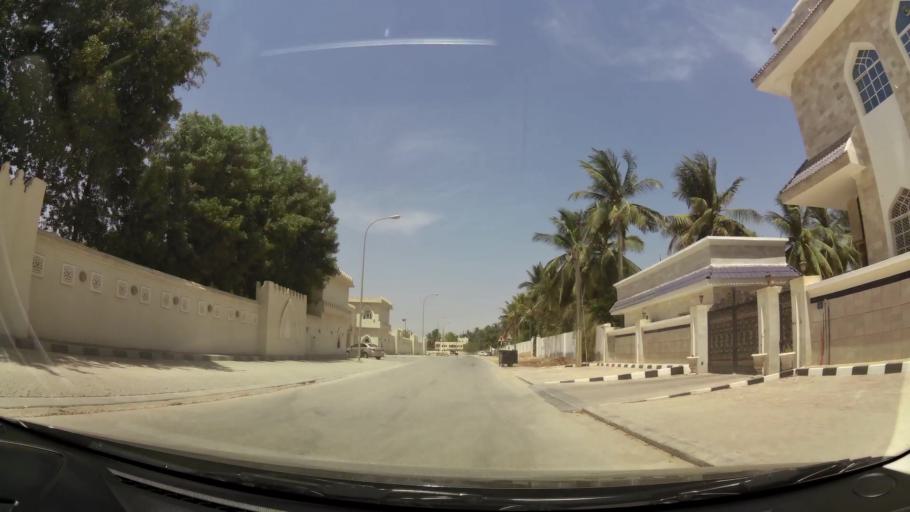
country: OM
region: Zufar
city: Salalah
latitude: 17.0552
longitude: 54.1552
